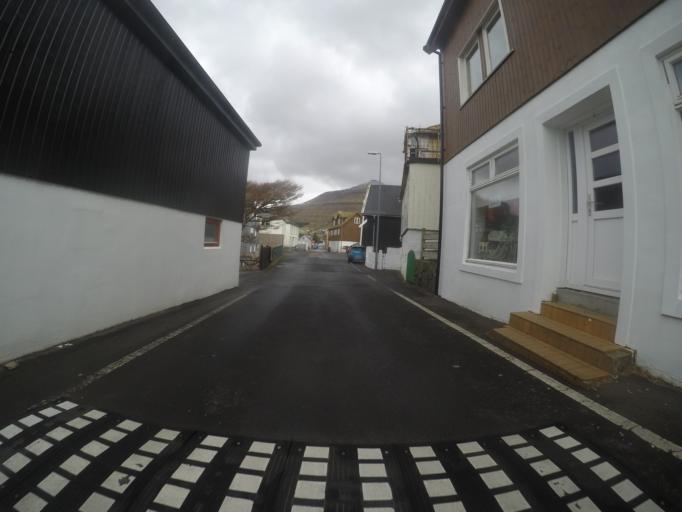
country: FO
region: Vagar
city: Midvagur
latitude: 62.0521
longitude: -7.1507
